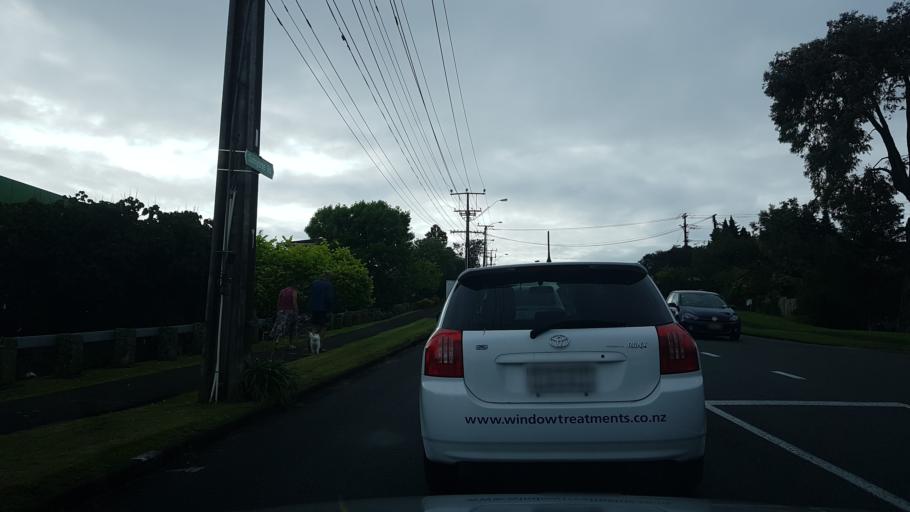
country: NZ
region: Auckland
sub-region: Auckland
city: North Shore
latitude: -36.7860
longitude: 174.7411
